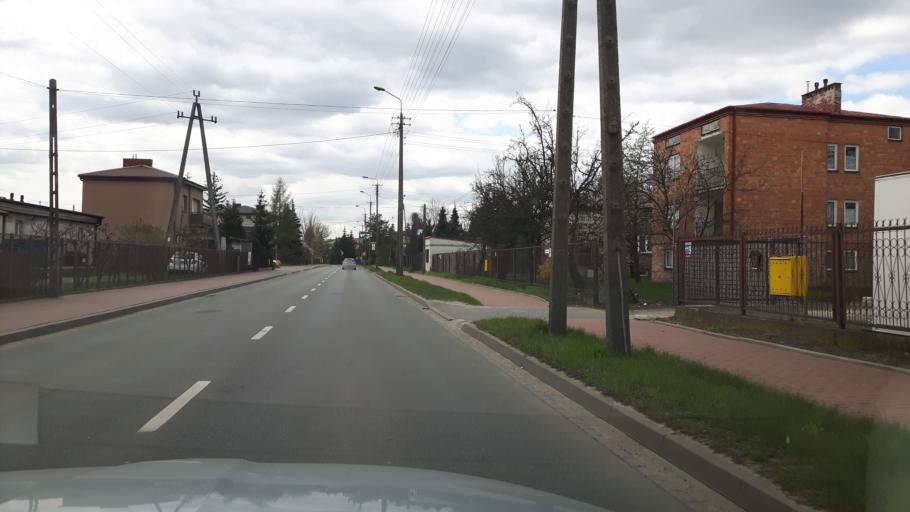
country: PL
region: Masovian Voivodeship
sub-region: Powiat wolominski
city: Wolomin
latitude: 52.3529
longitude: 21.2511
